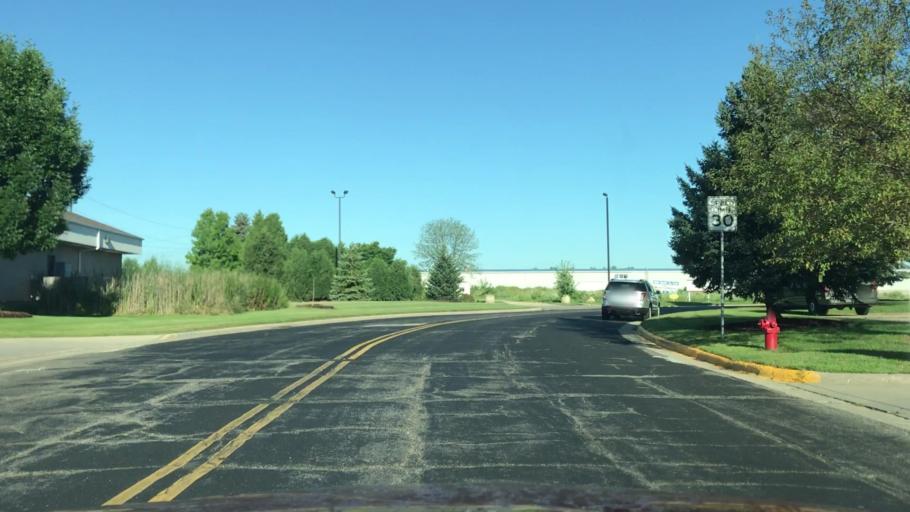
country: US
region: Wisconsin
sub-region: Dane County
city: Middleton
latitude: 43.0975
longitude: -89.5352
